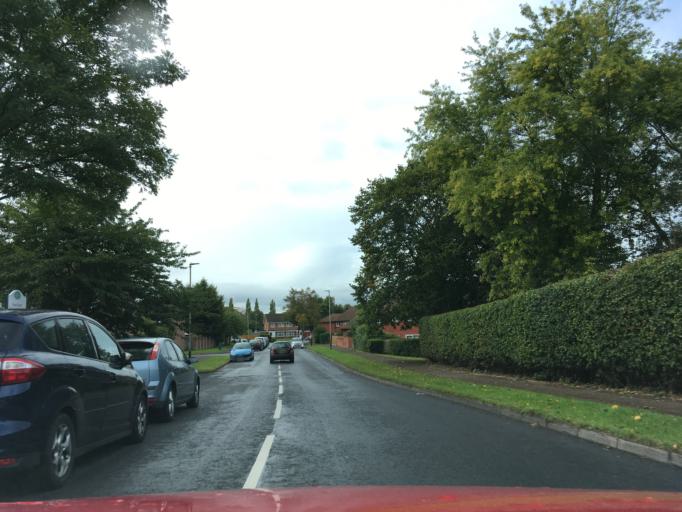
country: GB
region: England
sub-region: Gloucestershire
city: Uckington
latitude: 51.9041
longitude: -2.1226
